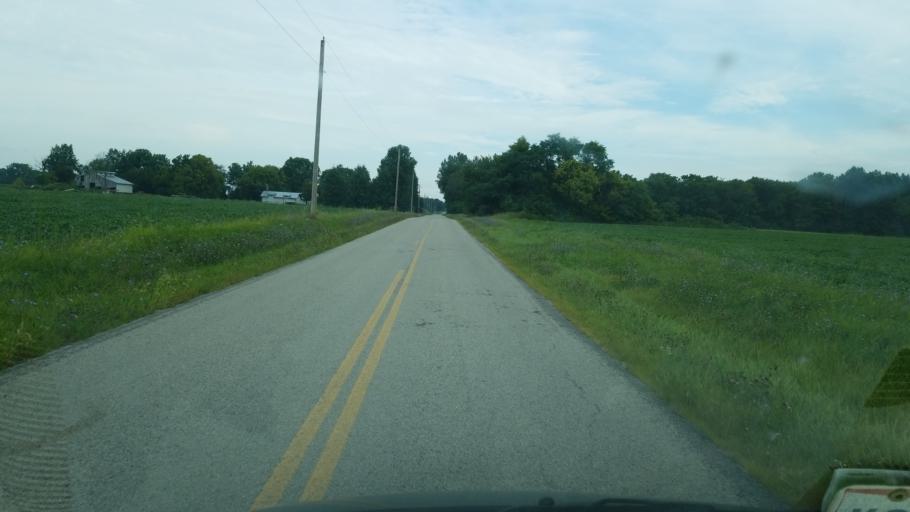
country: US
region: Ohio
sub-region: Seneca County
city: Tiffin
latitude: 41.0112
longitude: -83.0546
